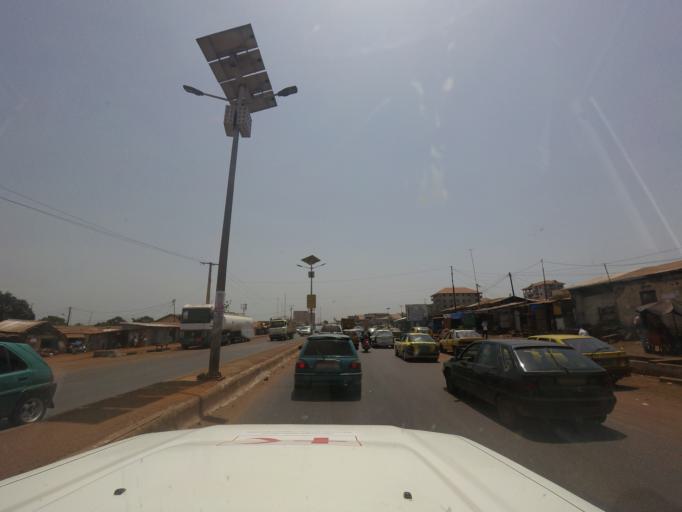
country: GN
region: Conakry
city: Conakry
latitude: 9.6347
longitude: -13.5711
